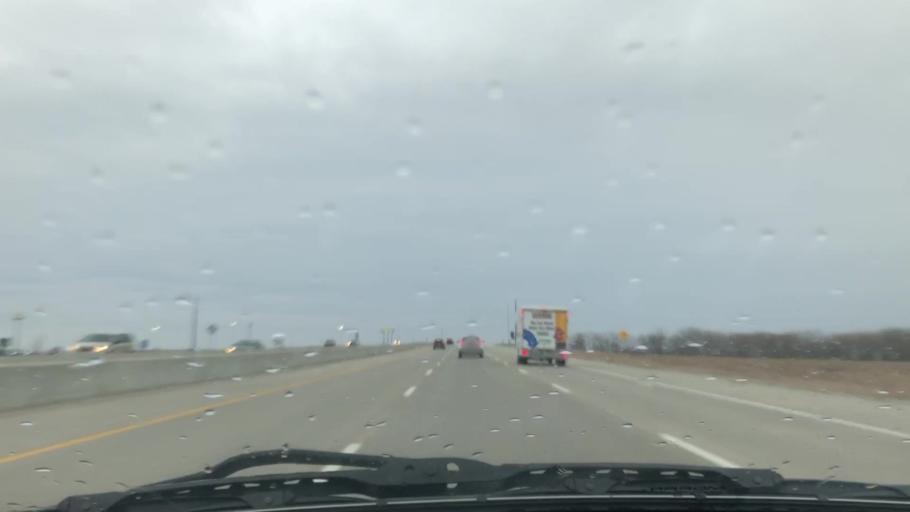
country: US
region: Iowa
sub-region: Polk County
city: Altoona
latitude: 41.6620
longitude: -93.4900
